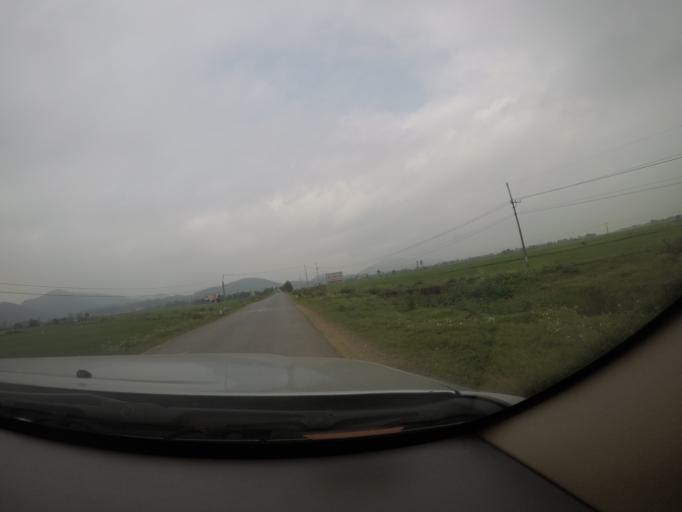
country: VN
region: Quang Binh
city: Ba Don
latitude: 17.6991
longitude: 106.4370
